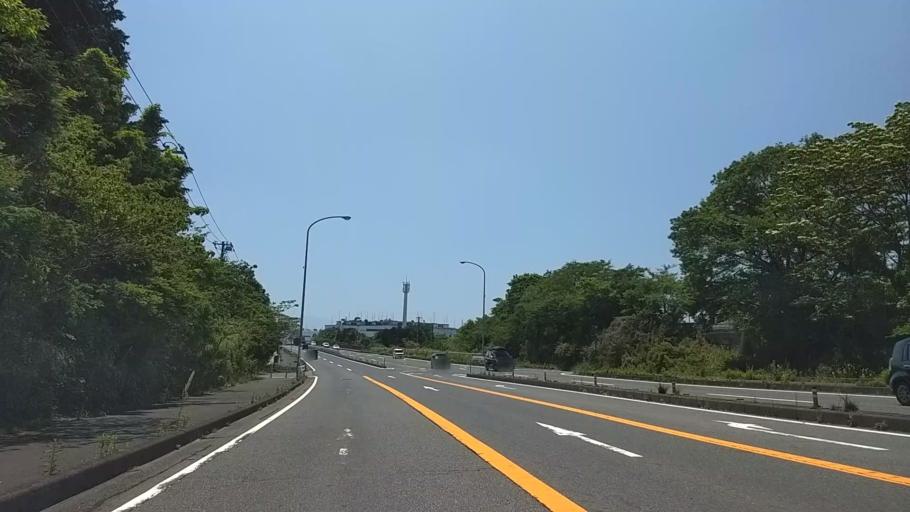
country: JP
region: Shizuoka
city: Gotemba
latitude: 35.2297
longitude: 138.9113
